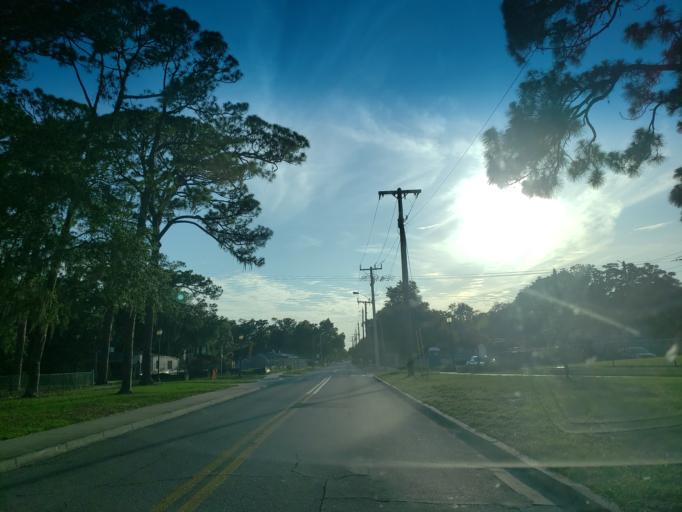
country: US
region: Florida
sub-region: Sarasota County
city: Sarasota
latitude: 27.3445
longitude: -82.5339
